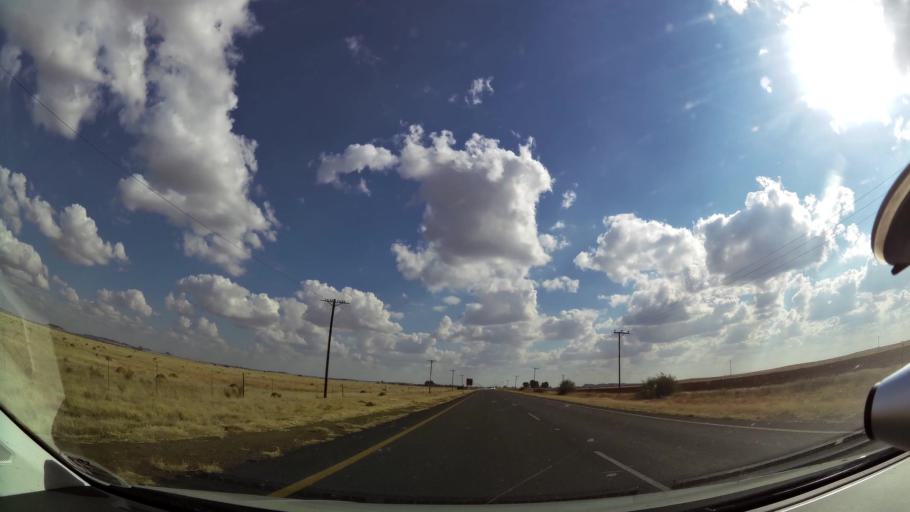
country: ZA
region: Orange Free State
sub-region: Xhariep District Municipality
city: Koffiefontein
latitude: -29.1298
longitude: 25.5113
